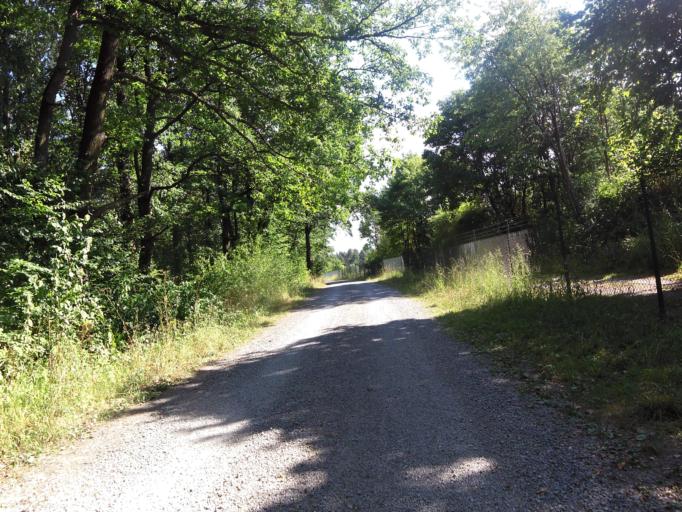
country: DE
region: Bavaria
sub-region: Regierungsbezirk Unterfranken
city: Gadheim
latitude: 49.8231
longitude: 9.9066
